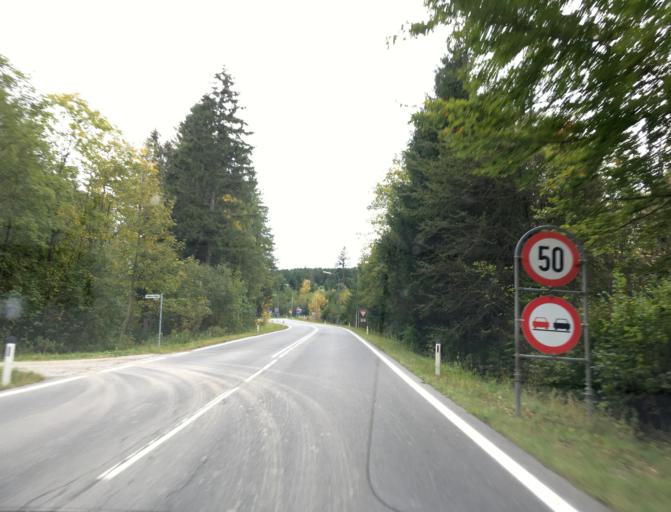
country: AT
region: Lower Austria
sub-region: Politischer Bezirk Neunkirchen
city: Thomasberg
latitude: 47.5488
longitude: 16.1438
